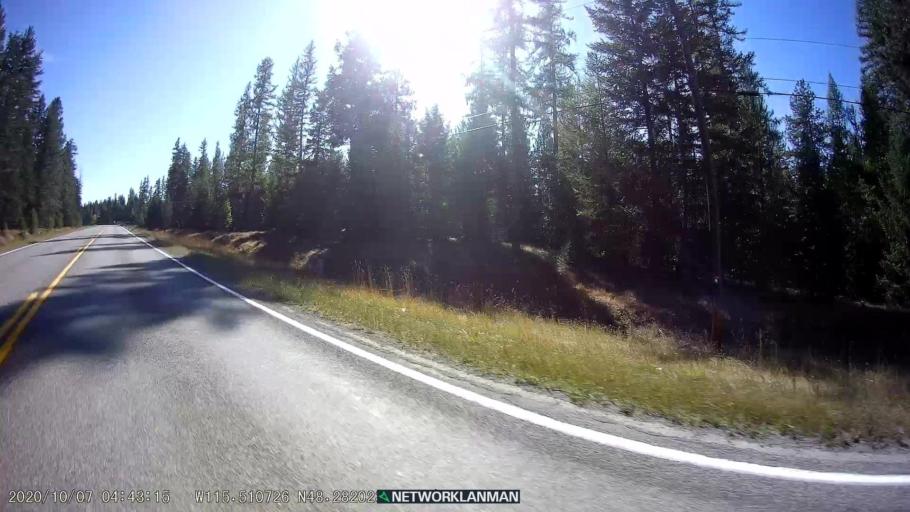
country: US
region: Montana
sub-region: Lincoln County
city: Libby
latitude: 48.2813
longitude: -115.5104
